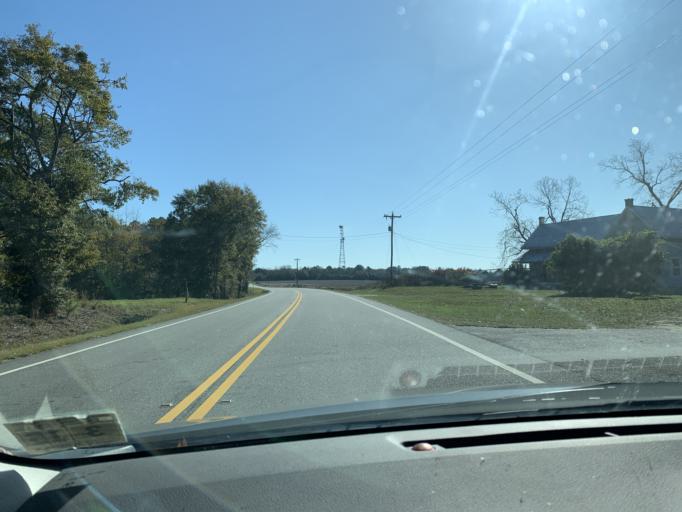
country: US
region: Georgia
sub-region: Ben Hill County
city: Fitzgerald
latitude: 31.7095
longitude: -83.1663
